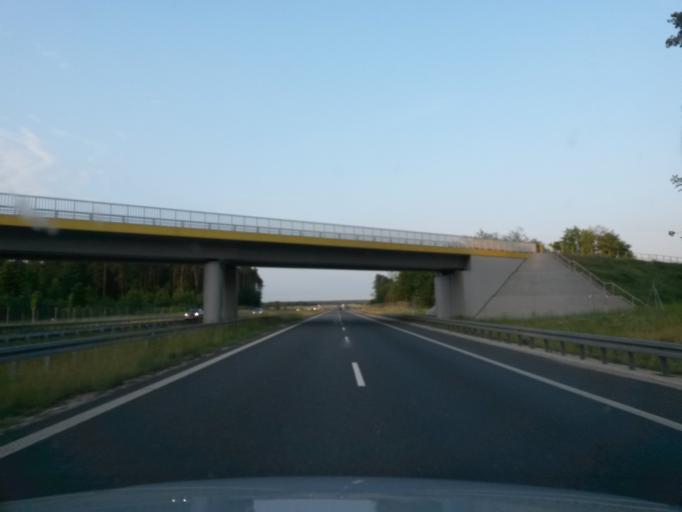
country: PL
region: Lodz Voivodeship
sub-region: Powiat wieruszowski
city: Sokolniki
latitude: 51.3206
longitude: 18.2996
